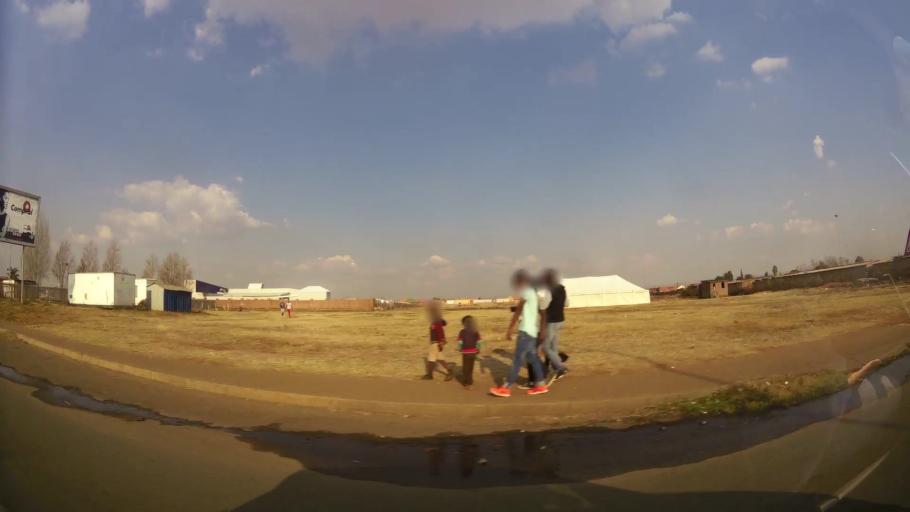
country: ZA
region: Gauteng
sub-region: Ekurhuleni Metropolitan Municipality
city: Germiston
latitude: -26.3594
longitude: 28.1922
